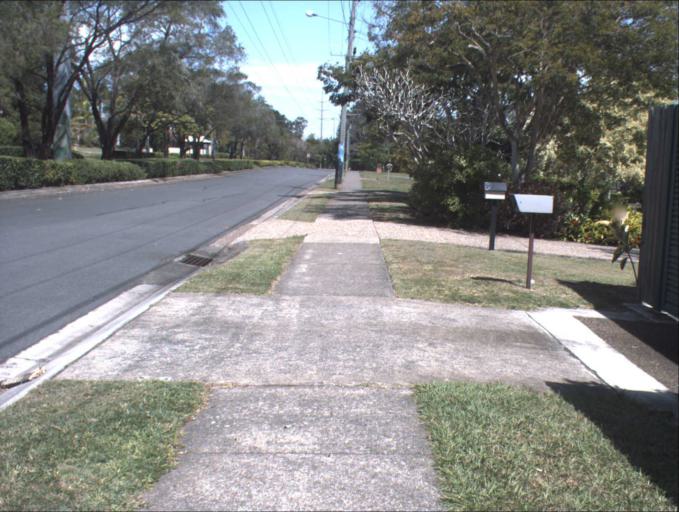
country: AU
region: Queensland
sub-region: Logan
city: Slacks Creek
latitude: -27.6390
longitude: 153.1507
